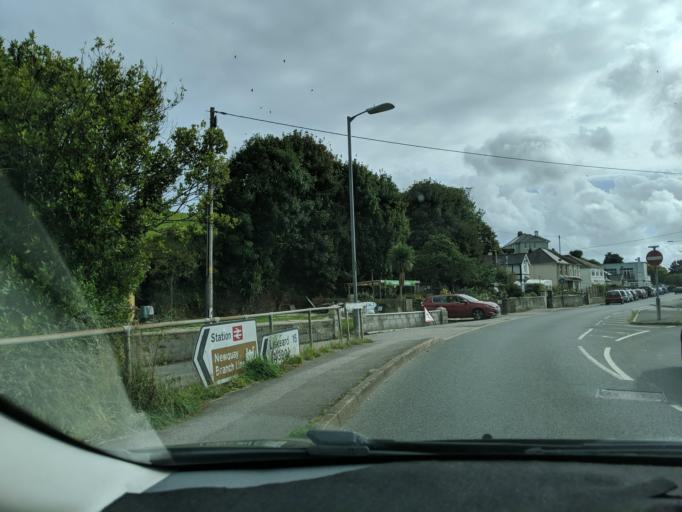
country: GB
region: England
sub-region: Cornwall
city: Par
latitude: 50.3542
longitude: -4.7005
